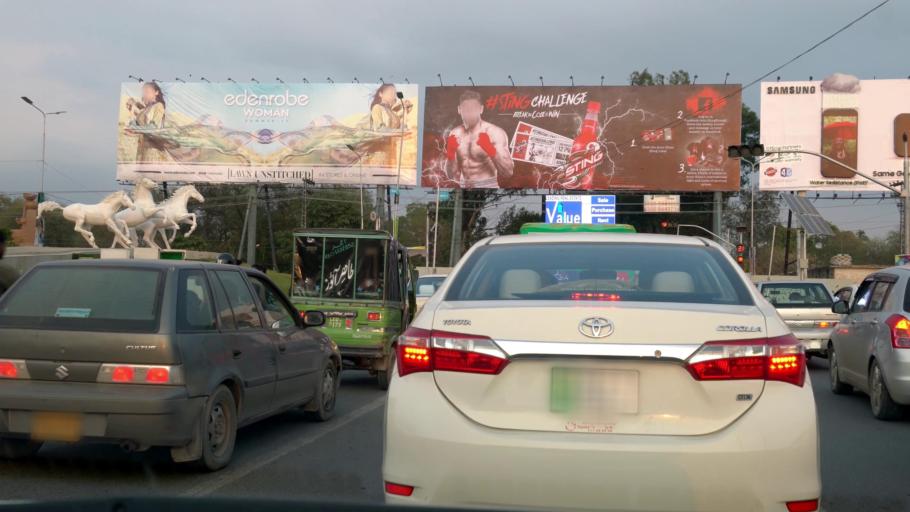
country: PK
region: Punjab
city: Lahore
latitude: 31.5015
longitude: 74.3684
